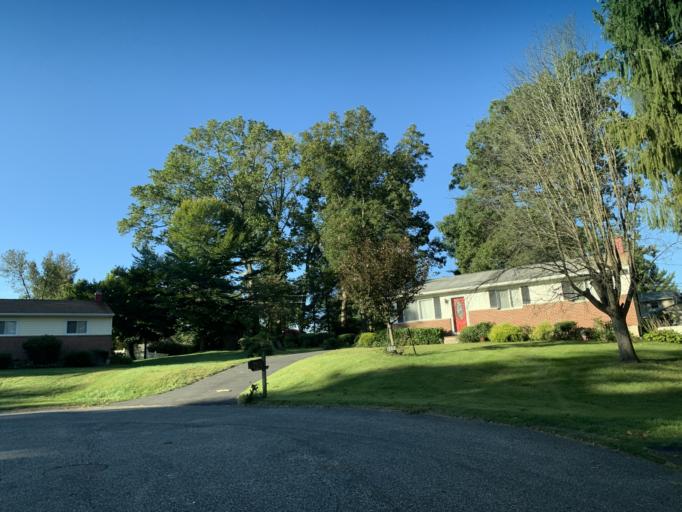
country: US
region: Maryland
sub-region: Harford County
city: Bel Air North
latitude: 39.5553
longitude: -76.3771
